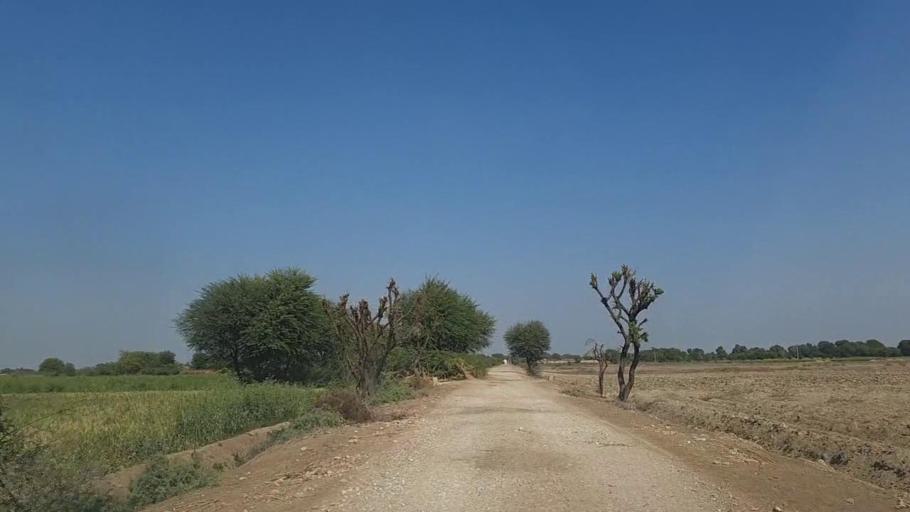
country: PK
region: Sindh
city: Digri
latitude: 25.1681
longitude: 69.1360
